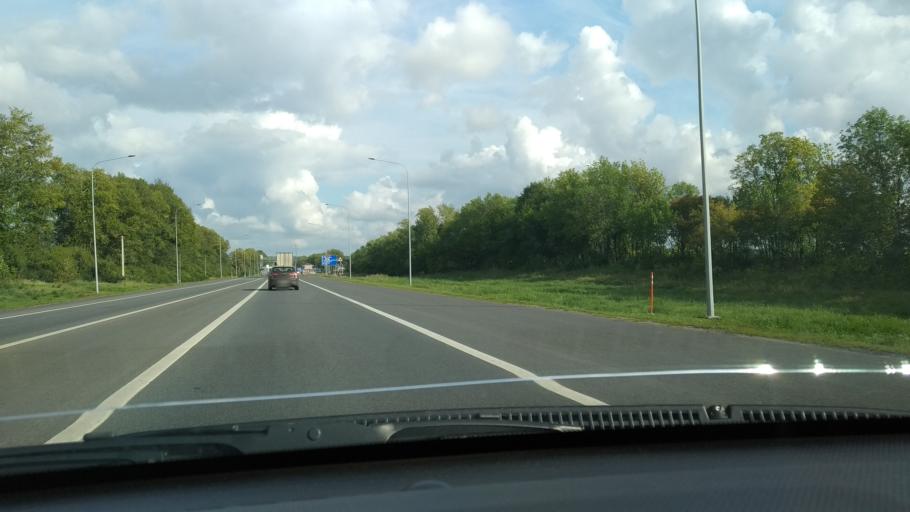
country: RU
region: Tatarstan
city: Stolbishchi
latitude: 55.6583
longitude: 49.3053
